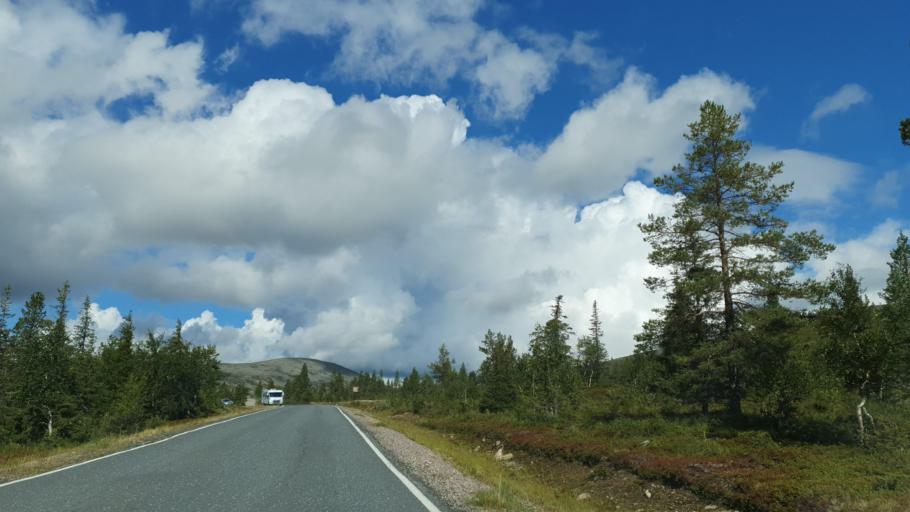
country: FI
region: Lapland
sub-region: Tunturi-Lappi
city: Muonio
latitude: 68.0434
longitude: 24.0681
